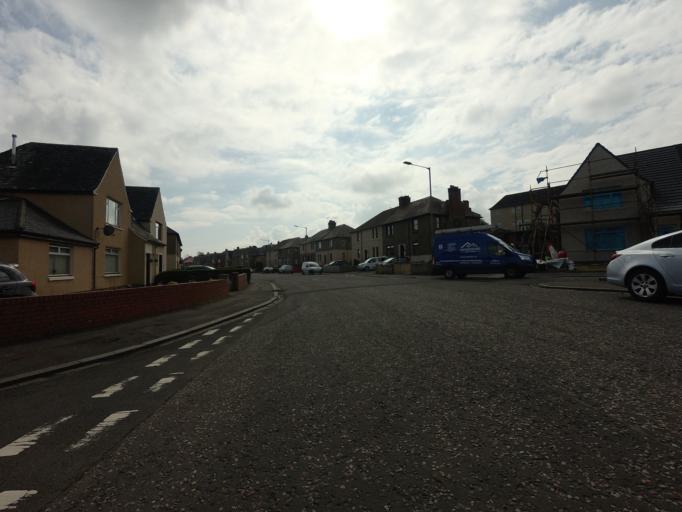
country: GB
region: Scotland
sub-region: Falkirk
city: Falkirk
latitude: 56.0019
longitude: -3.7689
